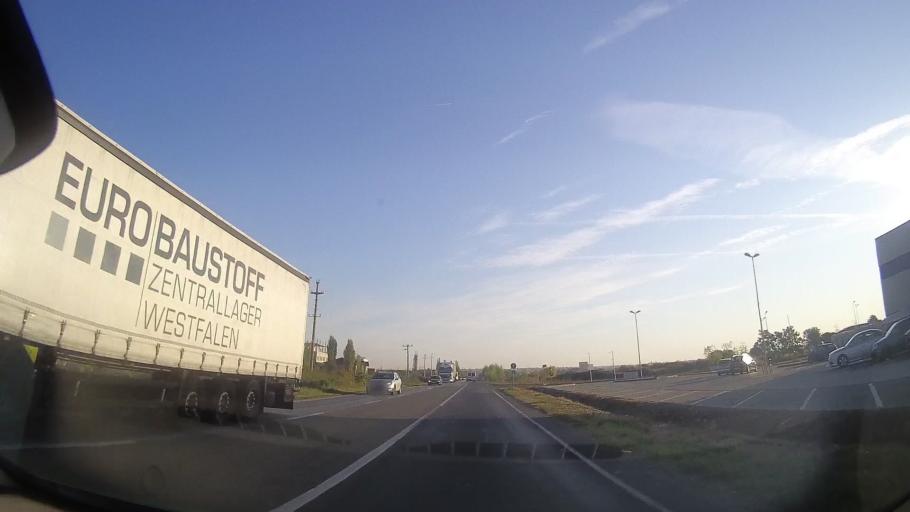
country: RO
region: Timis
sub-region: Comuna Giarmata
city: Giarmata
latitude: 45.8287
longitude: 21.2817
